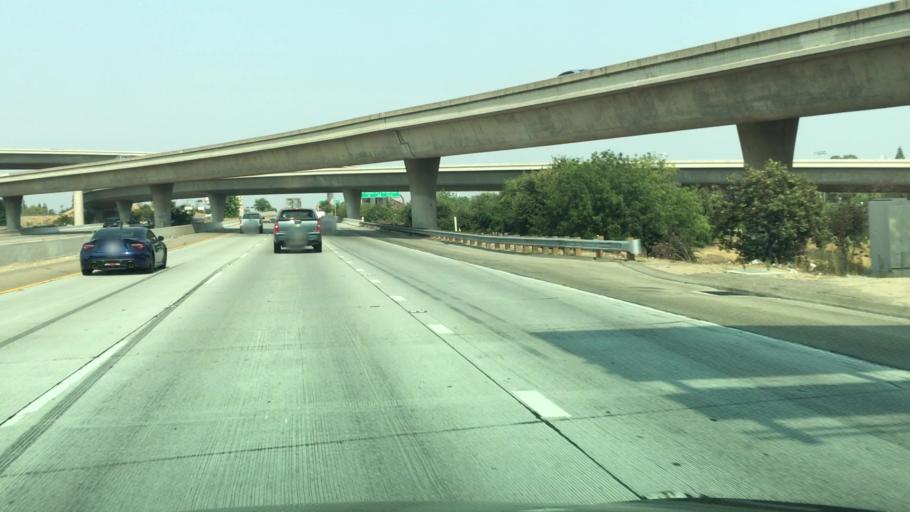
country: US
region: California
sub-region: Fresno County
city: Fresno
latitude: 36.7540
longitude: -119.7776
